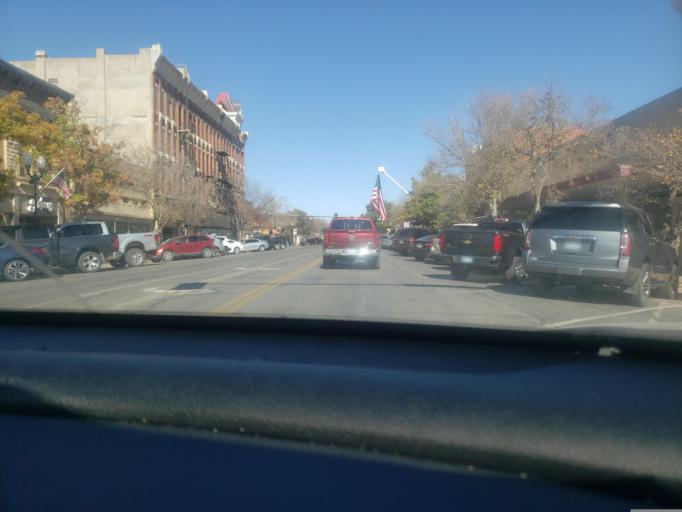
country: US
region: Kansas
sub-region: Finney County
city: Garden City
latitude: 37.9677
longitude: -100.8736
